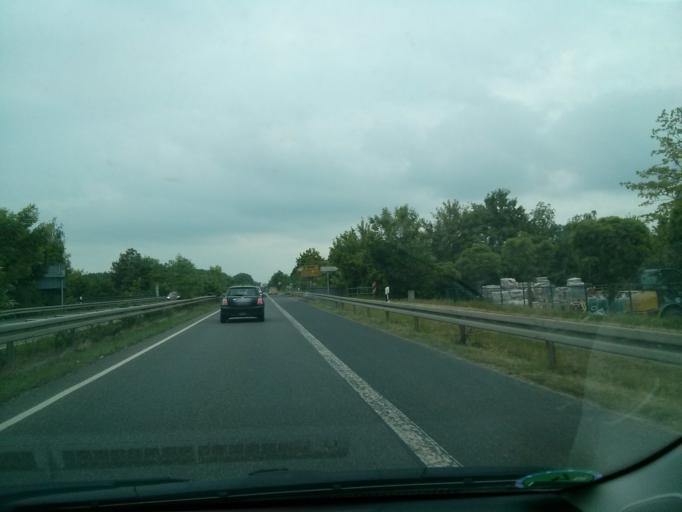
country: DE
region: North Rhine-Westphalia
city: Meckenheim
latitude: 50.6394
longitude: 7.0356
